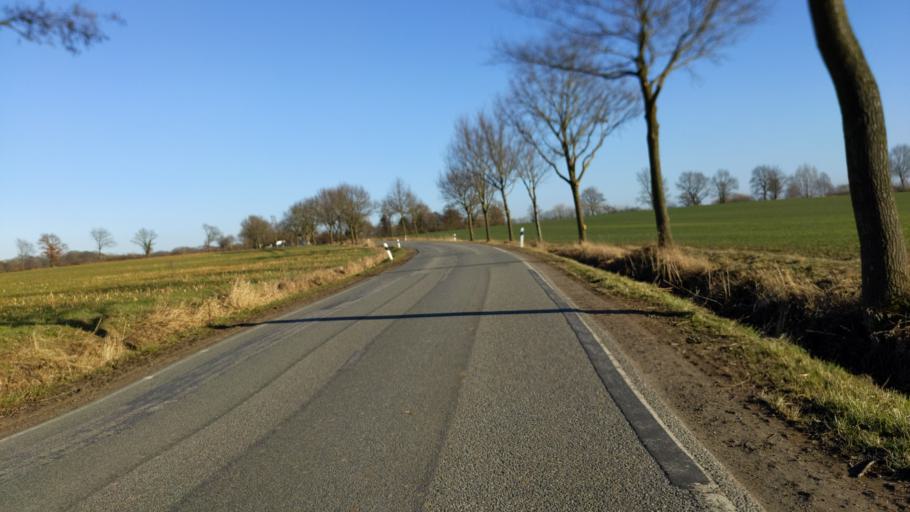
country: DE
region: Schleswig-Holstein
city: Susel
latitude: 54.0129
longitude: 10.6662
